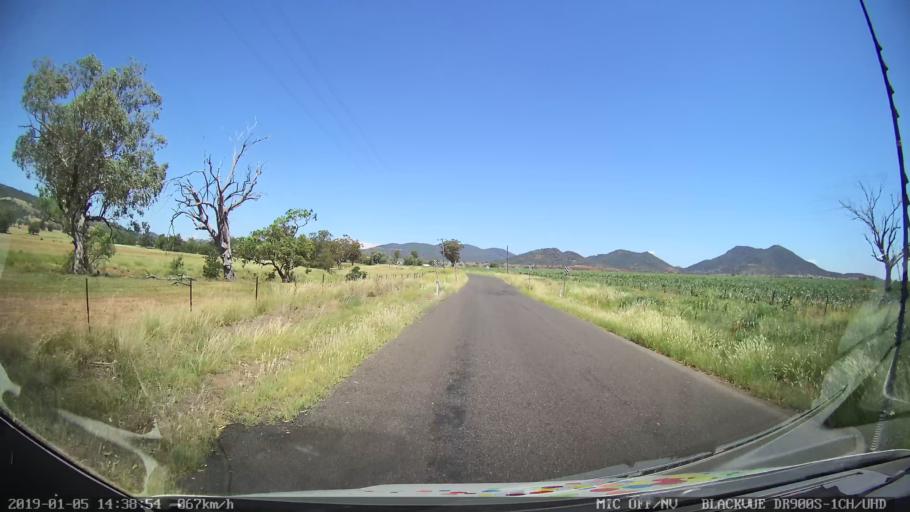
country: AU
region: New South Wales
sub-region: Tamworth Municipality
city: Phillip
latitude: -31.2521
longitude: 150.6948
